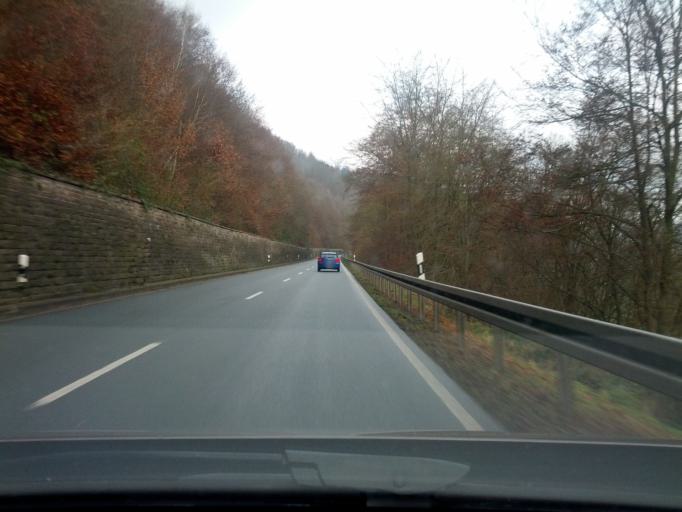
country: DE
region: Lower Saxony
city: Bodenfelde
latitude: 51.6046
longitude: 9.5375
